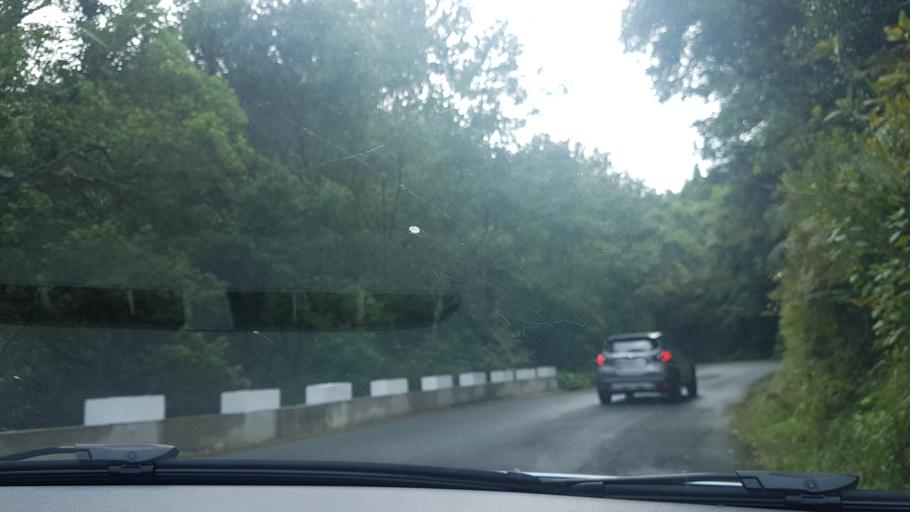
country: PT
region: Madeira
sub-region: Sao Vicente
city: Sao Vicente
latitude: 32.7623
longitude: -17.0207
